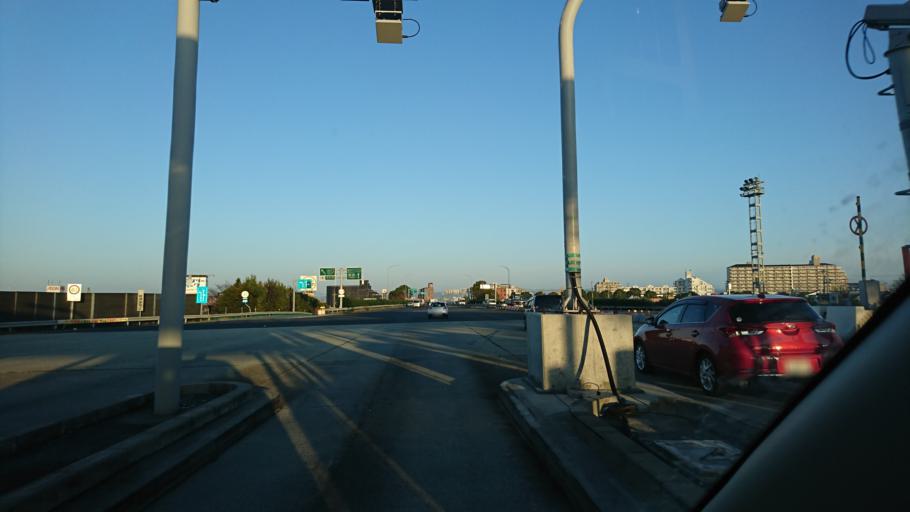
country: JP
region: Hyogo
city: Kakogawacho-honmachi
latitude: 34.7201
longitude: 134.8991
